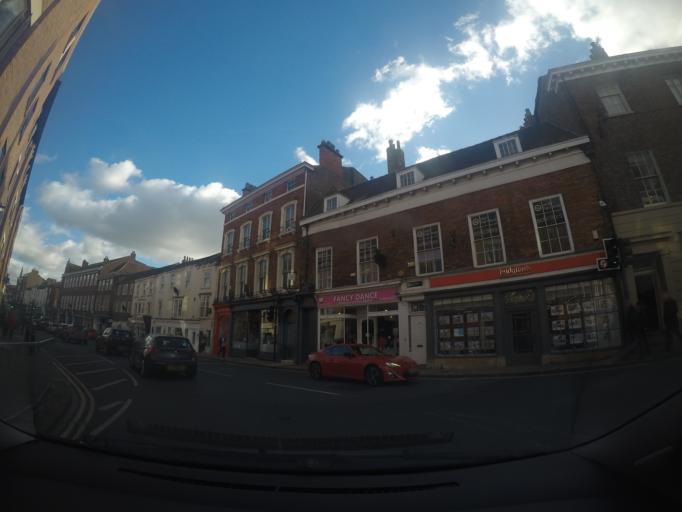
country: GB
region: England
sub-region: City of York
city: York
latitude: 53.9574
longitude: -1.0866
